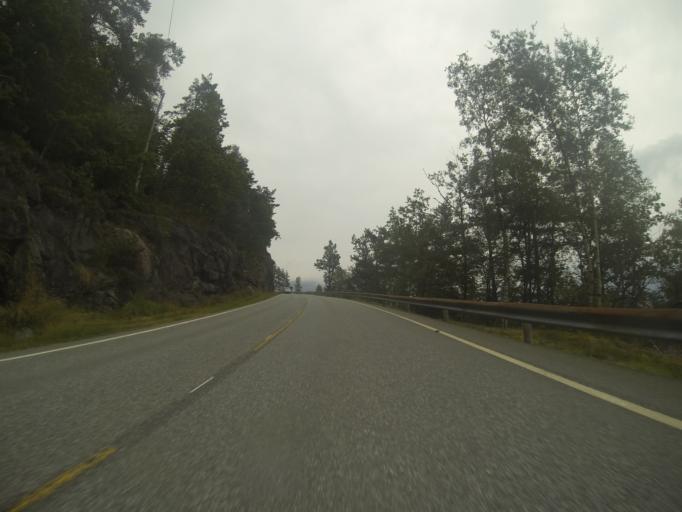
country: NO
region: Rogaland
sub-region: Suldal
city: Sand
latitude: 59.5328
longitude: 6.2534
